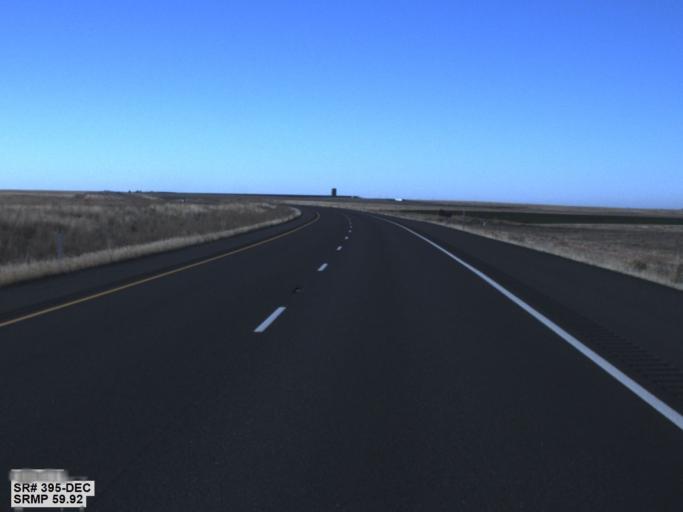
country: US
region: Washington
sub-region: Franklin County
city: Connell
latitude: 46.7198
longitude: -118.8350
